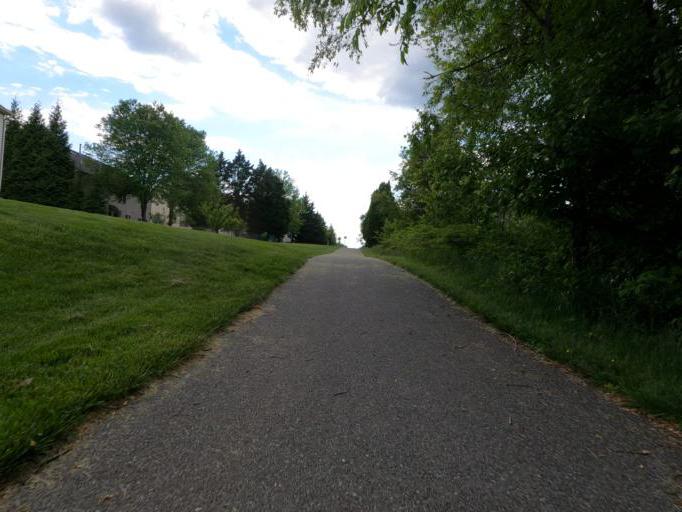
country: US
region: Maryland
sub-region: Montgomery County
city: Clarksburg
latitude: 39.2104
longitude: -77.2498
